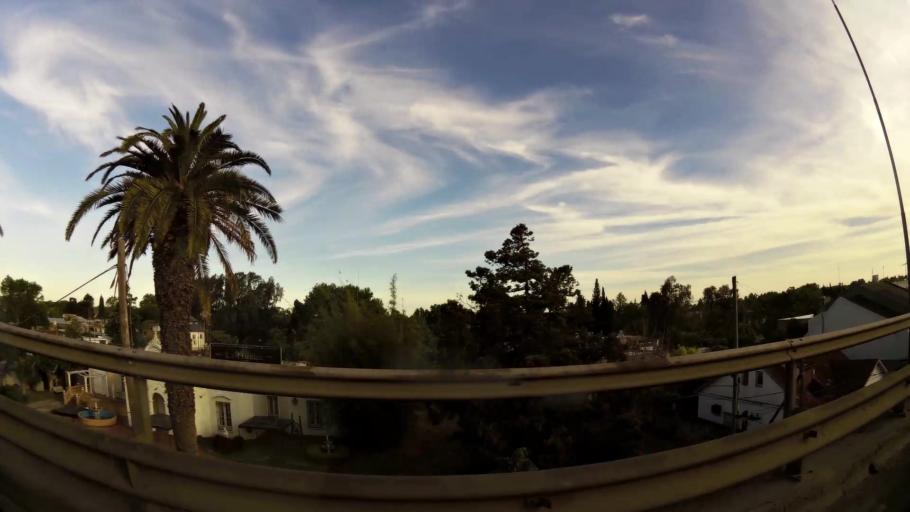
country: AR
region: Buenos Aires
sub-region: Partido de Almirante Brown
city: Adrogue
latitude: -34.8031
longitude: -58.3330
